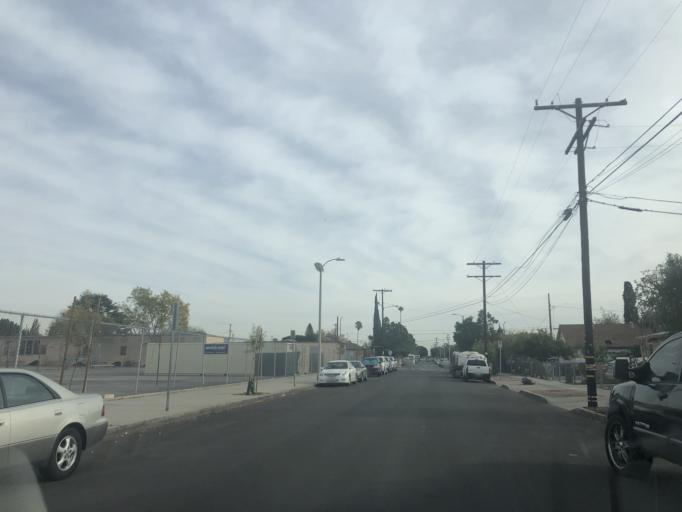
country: US
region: California
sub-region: Los Angeles County
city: San Fernando
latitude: 34.2677
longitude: -118.4327
